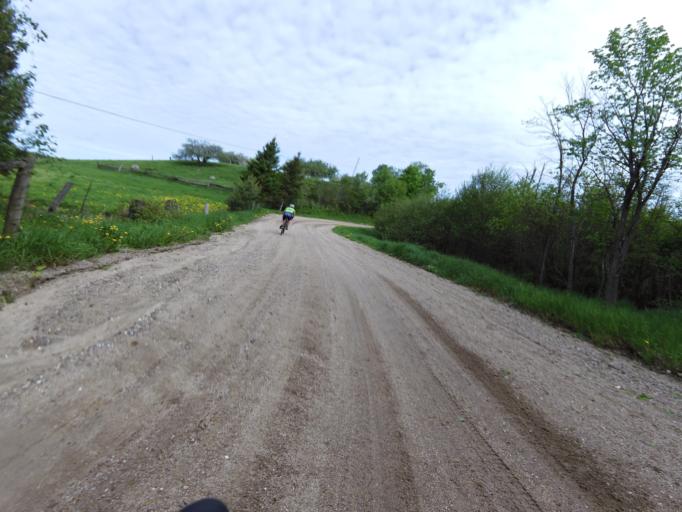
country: CA
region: Quebec
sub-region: Outaouais
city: Wakefield
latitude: 45.7410
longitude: -75.8899
